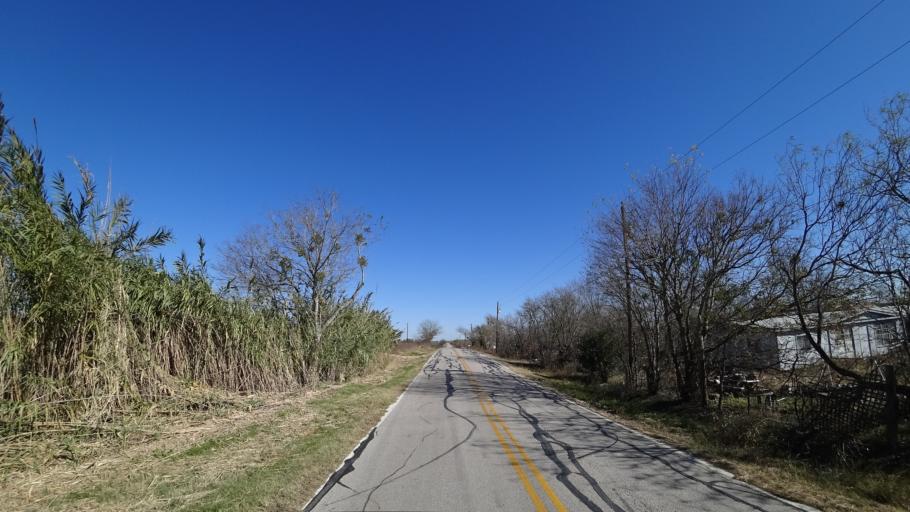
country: US
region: Texas
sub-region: Travis County
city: Garfield
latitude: 30.1035
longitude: -97.6304
